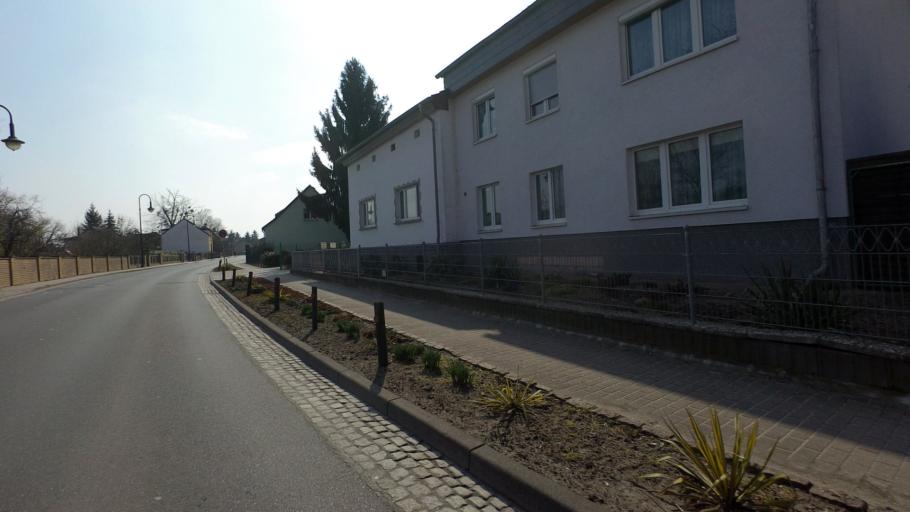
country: DE
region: Brandenburg
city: Werder
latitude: 52.3705
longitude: 12.9373
